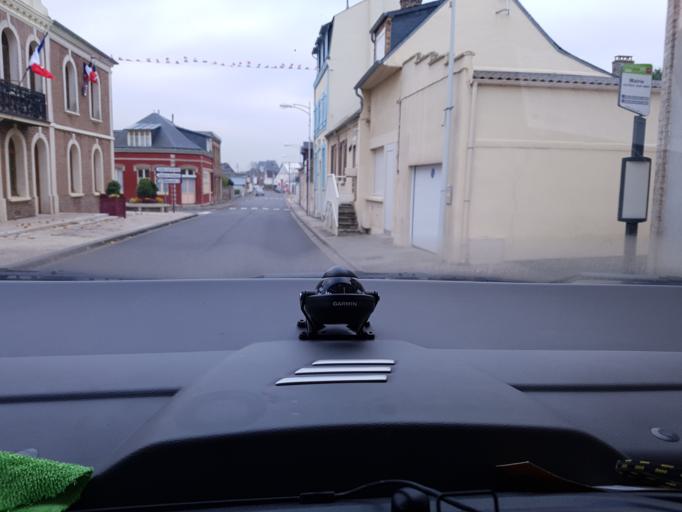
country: FR
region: Picardie
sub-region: Departement de la Somme
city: Cayeux-sur-Mer
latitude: 50.1794
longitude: 1.4931
